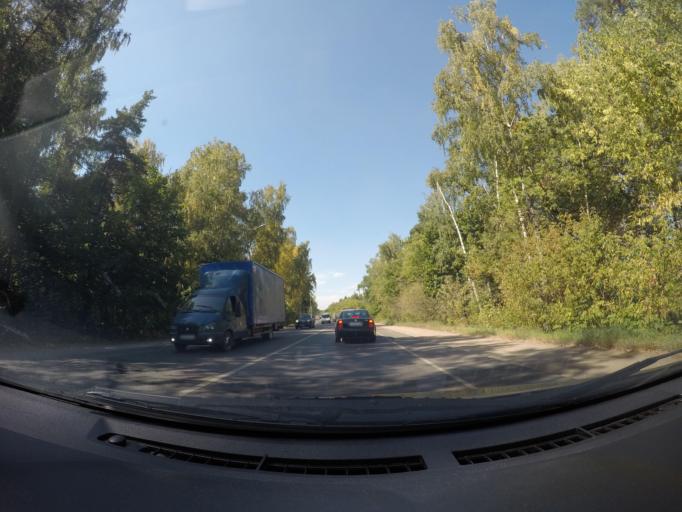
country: RU
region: Moskovskaya
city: Malakhovka
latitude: 55.6587
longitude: 38.0340
